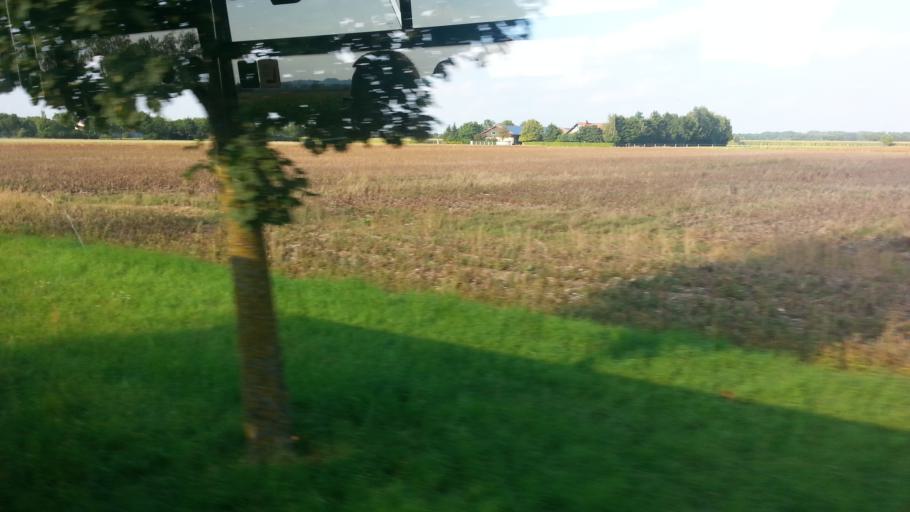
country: DE
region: Bavaria
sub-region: Upper Bavaria
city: Neufahrn bei Freising
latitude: 48.3013
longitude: 11.6694
